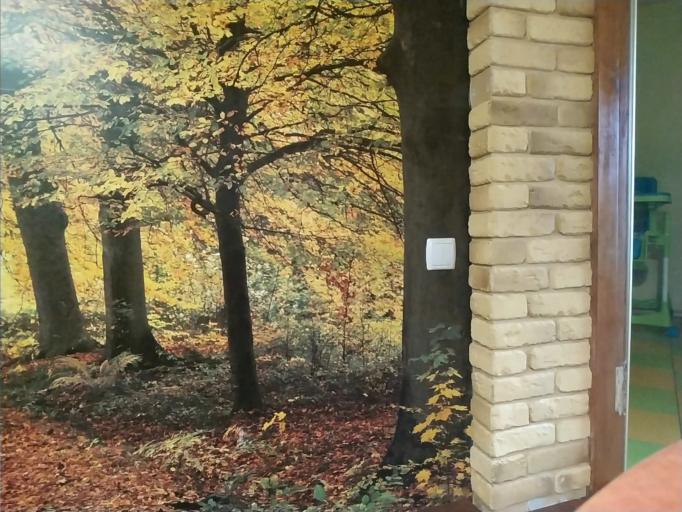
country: RU
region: Tverskaya
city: Likhoslavl'
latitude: 56.9527
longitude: 35.6269
